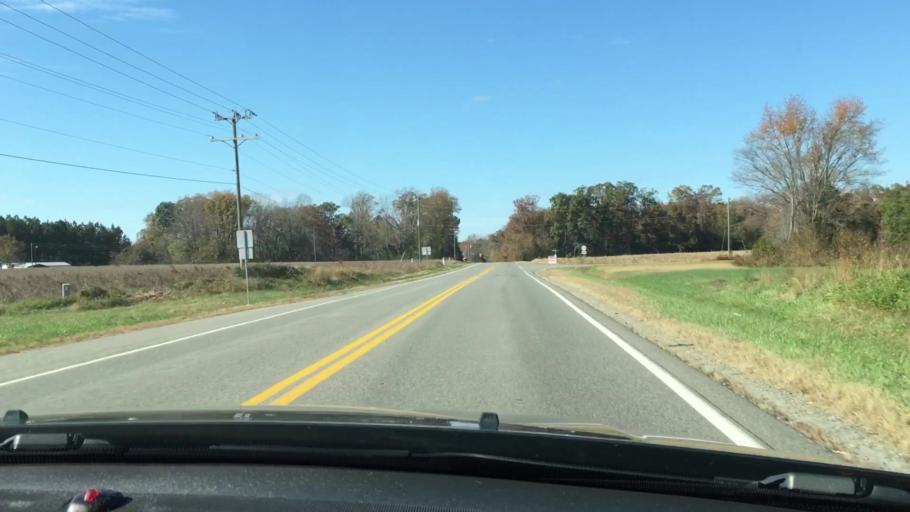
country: US
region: Virginia
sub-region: King William County
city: King William
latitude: 37.7095
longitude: -77.0559
